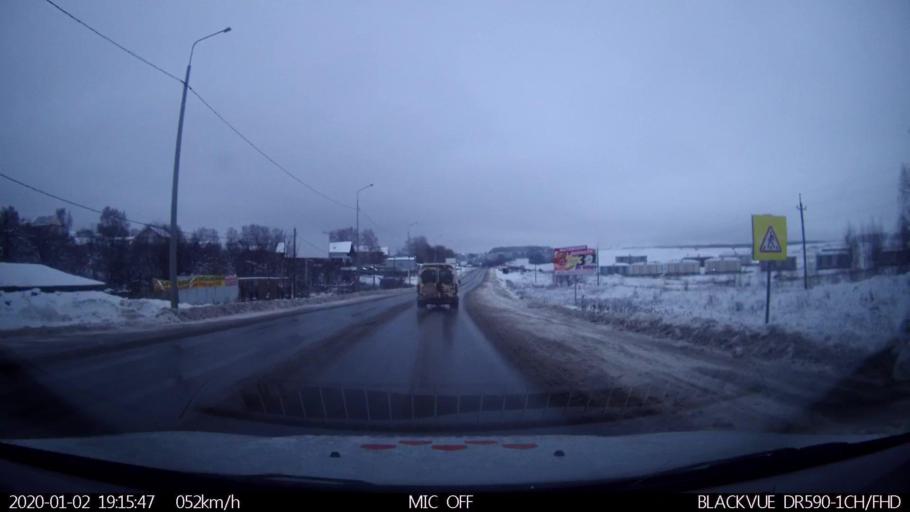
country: RU
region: Nizjnij Novgorod
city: Burevestnik
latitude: 56.2122
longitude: 43.8890
